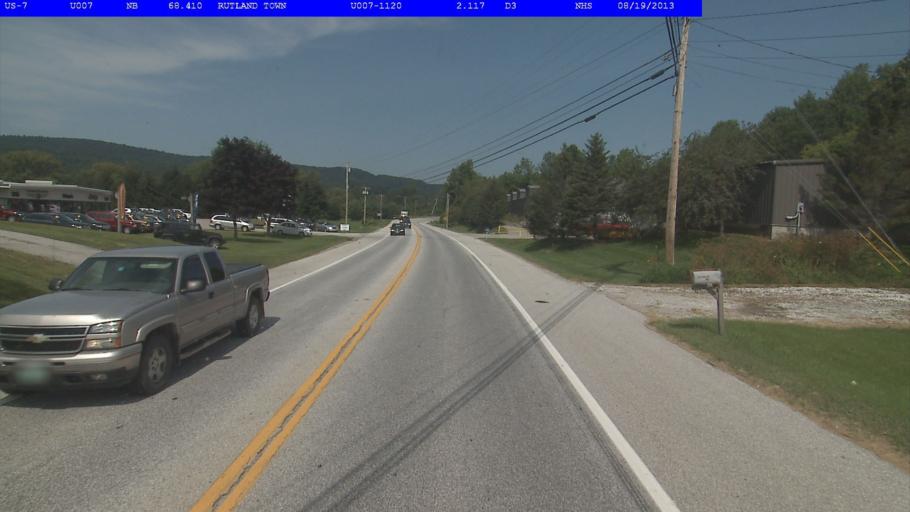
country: US
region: Vermont
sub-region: Rutland County
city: Rutland
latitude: 43.6424
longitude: -72.9813
